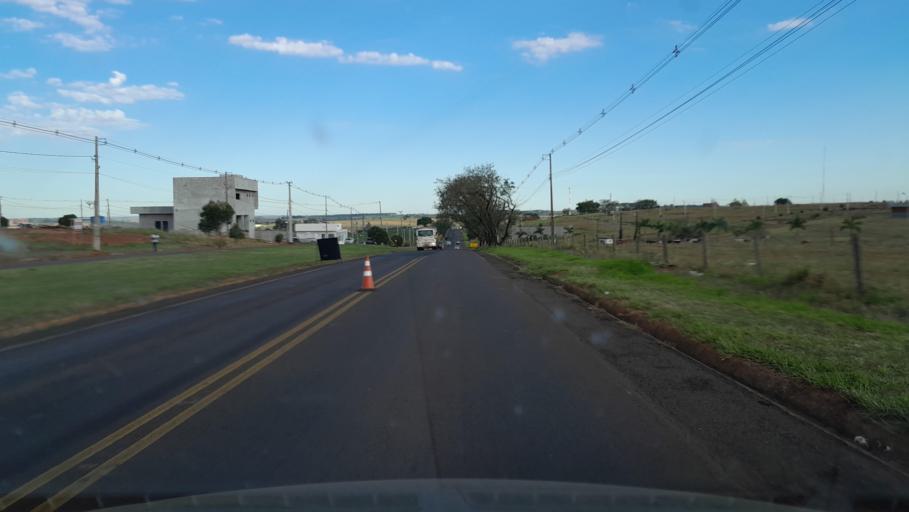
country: BR
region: Parana
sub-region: Umuarama
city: Umuarama
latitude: -23.7617
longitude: -53.2707
